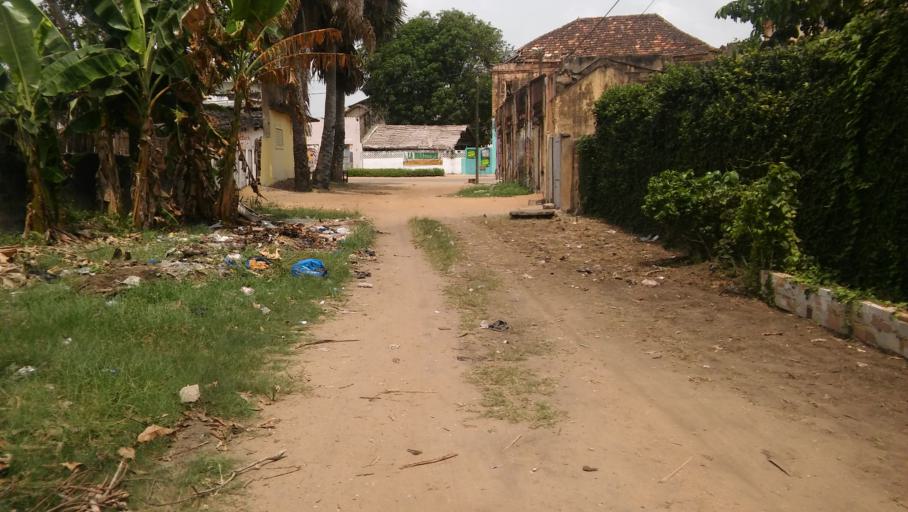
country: CI
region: Sud-Comoe
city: Grand-Bassam
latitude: 5.1947
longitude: -3.7313
